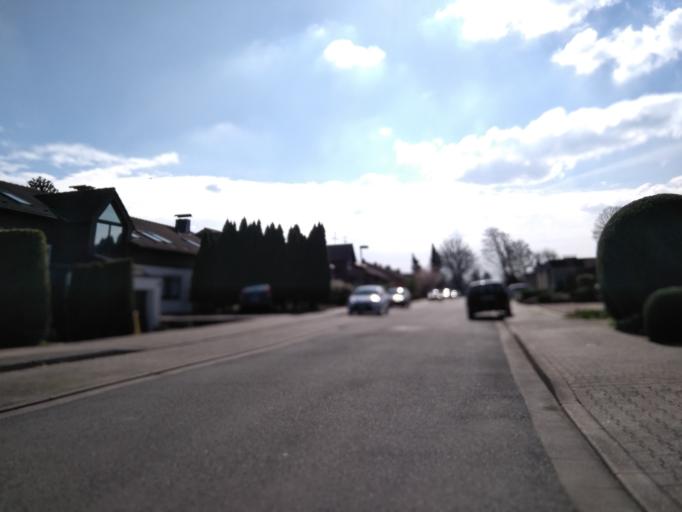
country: DE
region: North Rhine-Westphalia
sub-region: Regierungsbezirk Munster
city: Gladbeck
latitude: 51.5849
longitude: 7.0158
